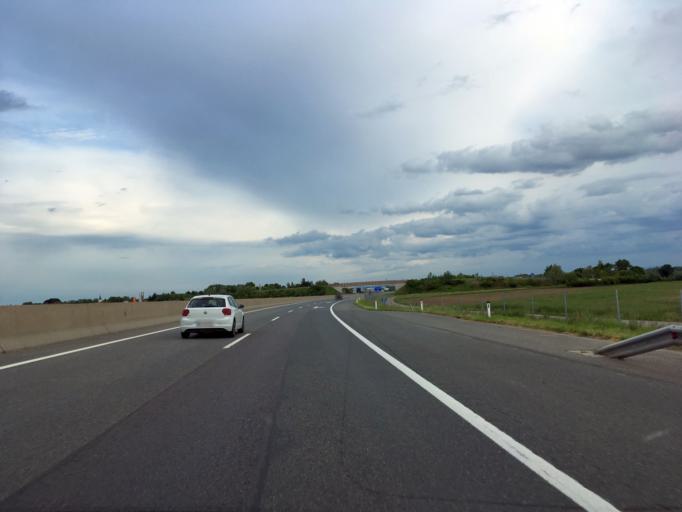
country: AT
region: Lower Austria
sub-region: Politischer Bezirk Tulln
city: Kirchberg am Wagram
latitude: 48.3958
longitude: 15.9151
